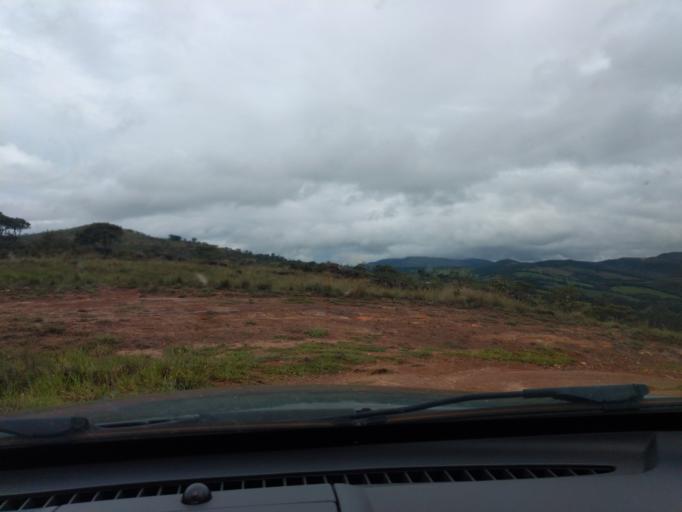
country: BR
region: Minas Gerais
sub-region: Lavras
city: Lavras
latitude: -21.5193
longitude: -44.9294
